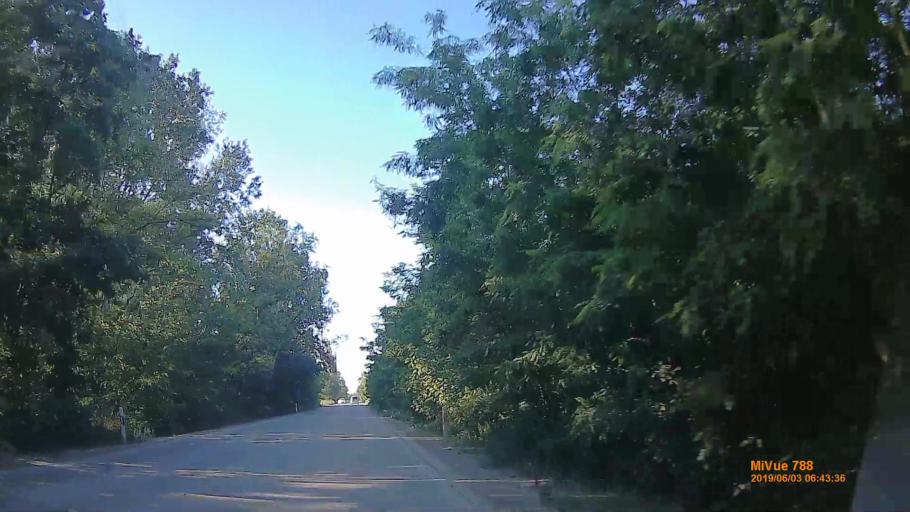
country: HU
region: Pest
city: Bugyi
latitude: 47.2534
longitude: 19.1257
